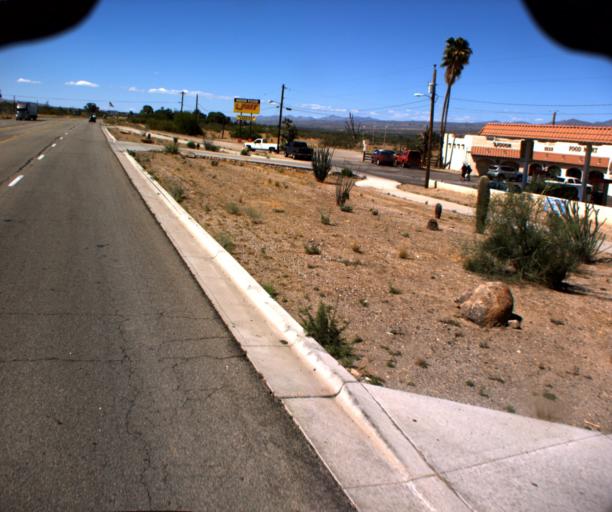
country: US
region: Arizona
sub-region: Yavapai County
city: Bagdad
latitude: 34.7039
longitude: -113.6113
